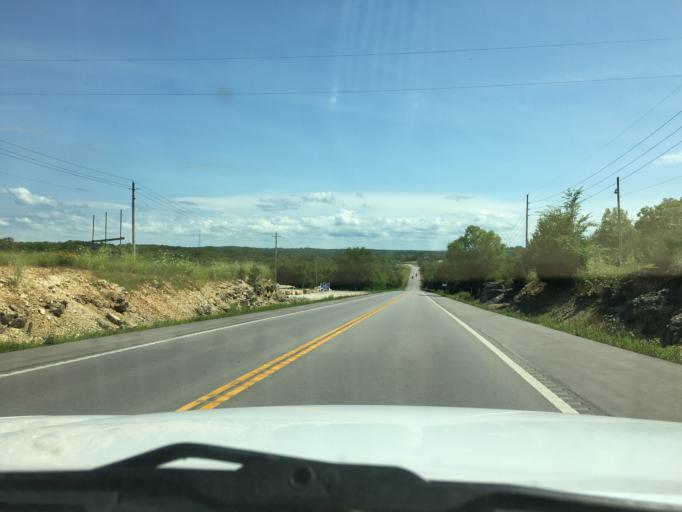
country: US
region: Missouri
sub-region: Franklin County
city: Union
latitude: 38.4705
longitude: -91.0057
